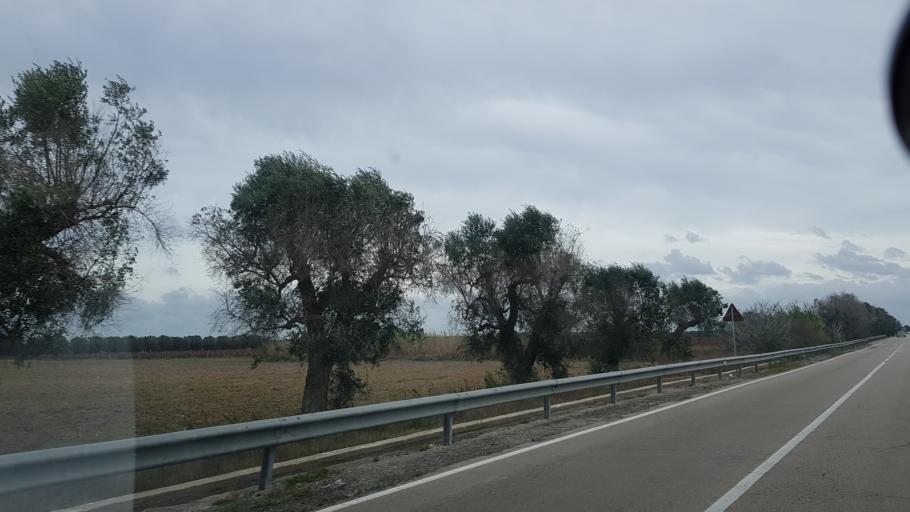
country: IT
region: Apulia
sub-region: Provincia di Brindisi
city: San Donaci
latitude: 40.4054
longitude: 17.8931
